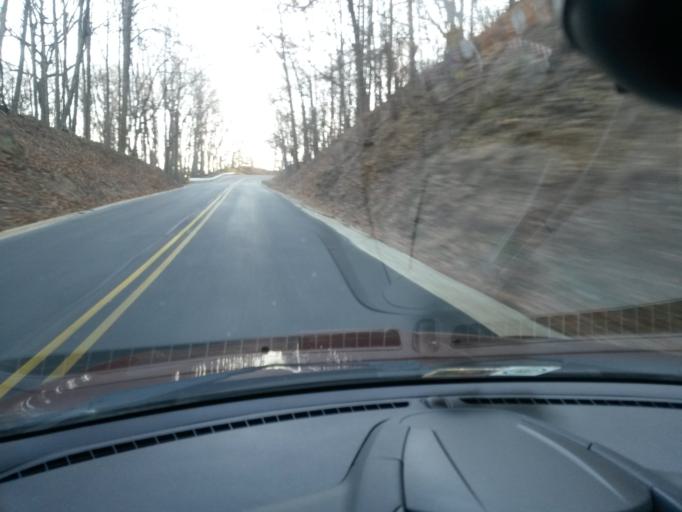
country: US
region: Virginia
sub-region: City of Buena Vista
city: Buena Vista
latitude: 37.7517
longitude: -79.2849
